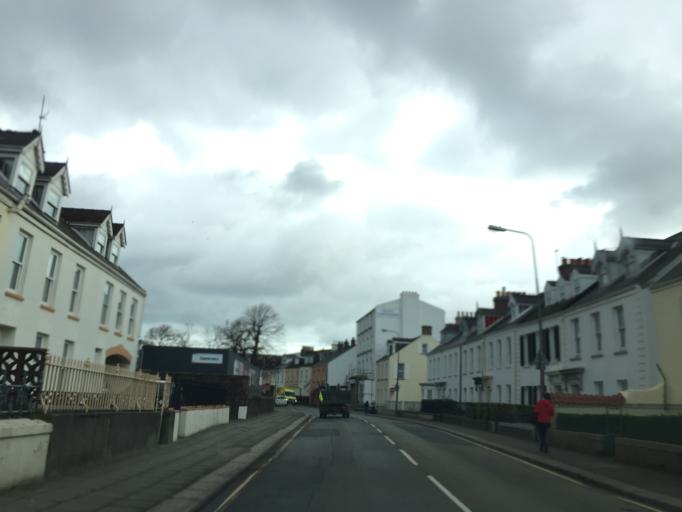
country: JE
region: St Helier
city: Saint Helier
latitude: 49.1897
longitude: -2.1106
